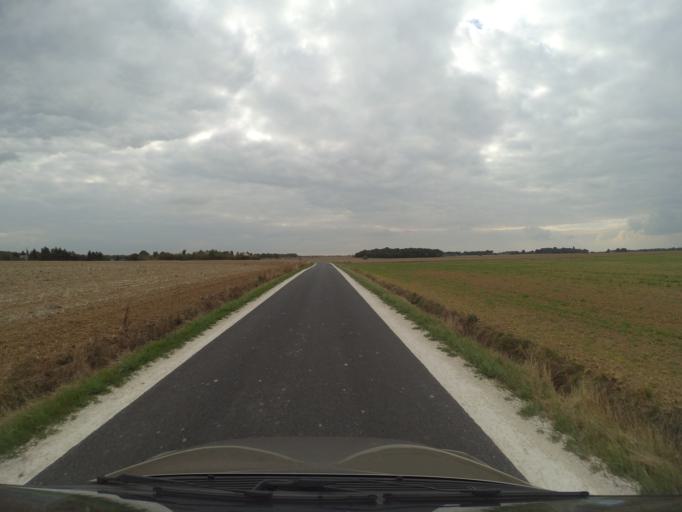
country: FR
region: Centre
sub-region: Departement d'Indre-et-Loire
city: Poce-sur-Cisse
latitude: 47.5057
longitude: 0.9745
